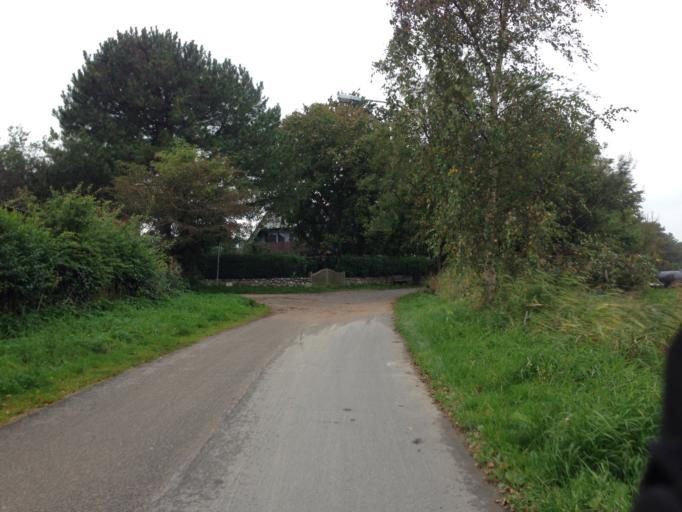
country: DE
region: Schleswig-Holstein
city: Wyk auf Fohr
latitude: 54.6938
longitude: 8.5649
